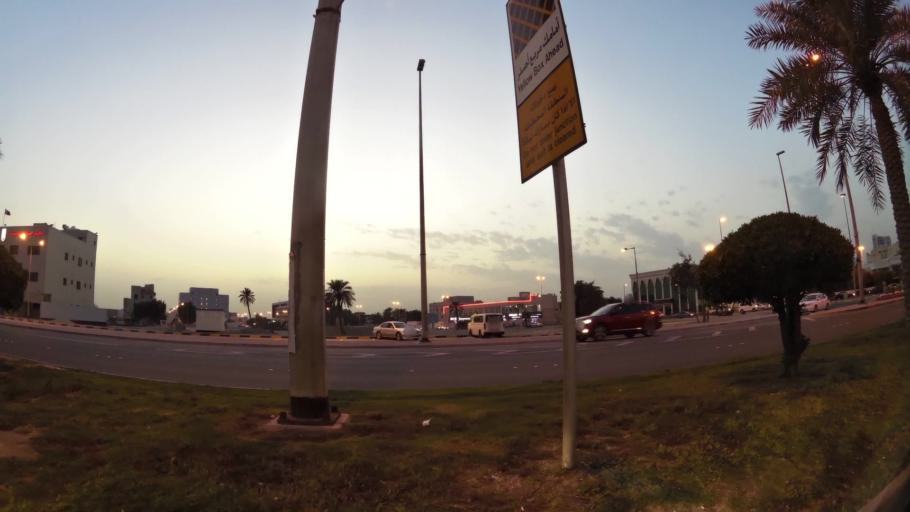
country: BH
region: Manama
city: Jidd Hafs
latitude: 26.2159
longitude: 50.5653
